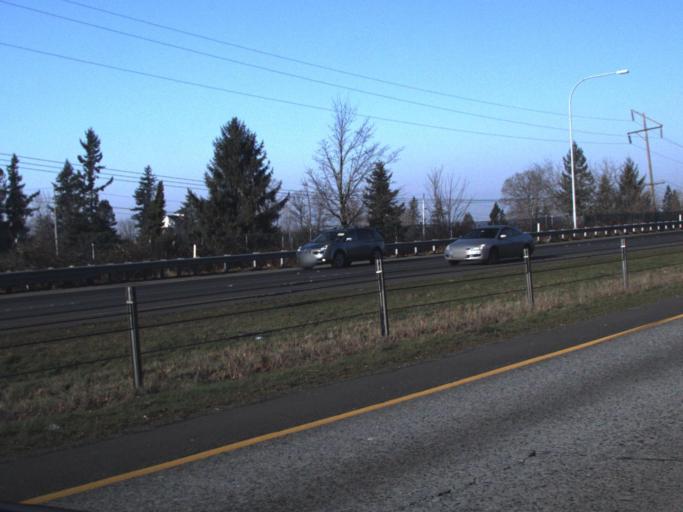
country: US
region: Washington
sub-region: Whatcom County
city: Bellingham
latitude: 48.7413
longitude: -122.4674
